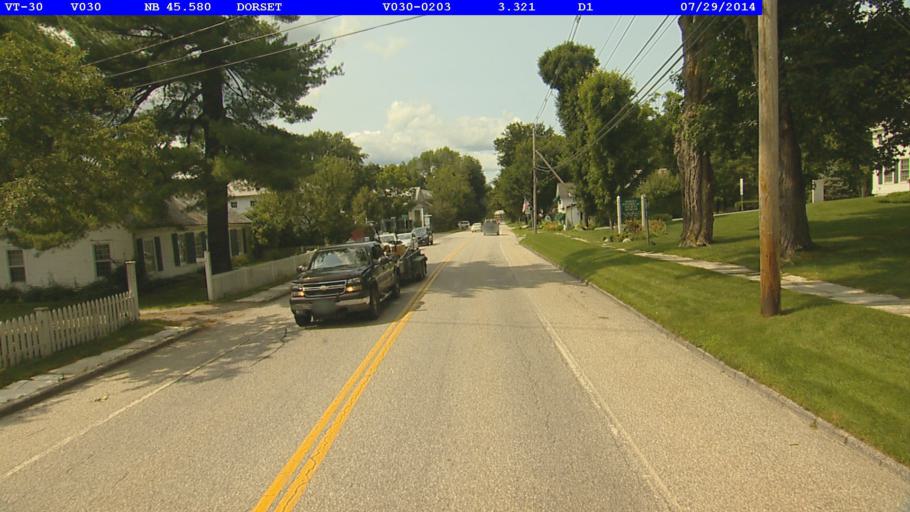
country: US
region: Vermont
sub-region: Bennington County
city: Manchester Center
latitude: 43.2543
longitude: -73.0982
